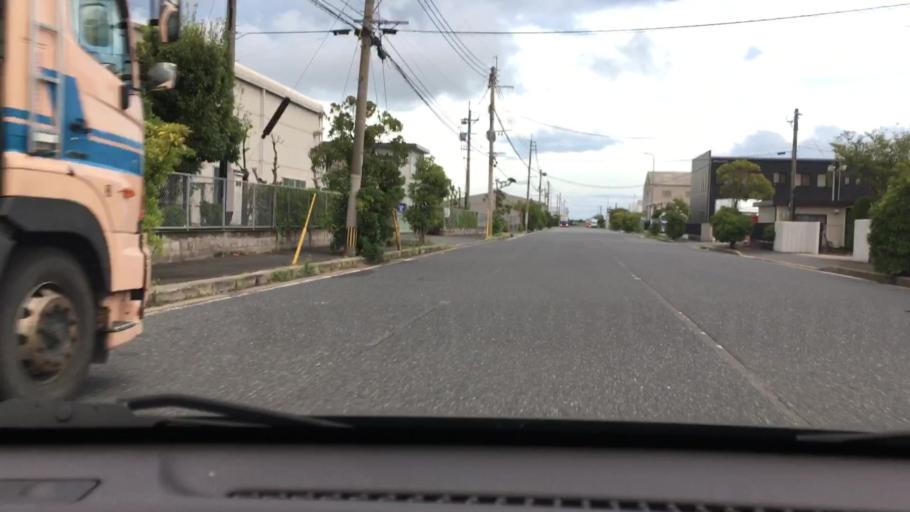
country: JP
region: Yamaguchi
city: Shimonoseki
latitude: 33.8885
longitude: 130.9904
